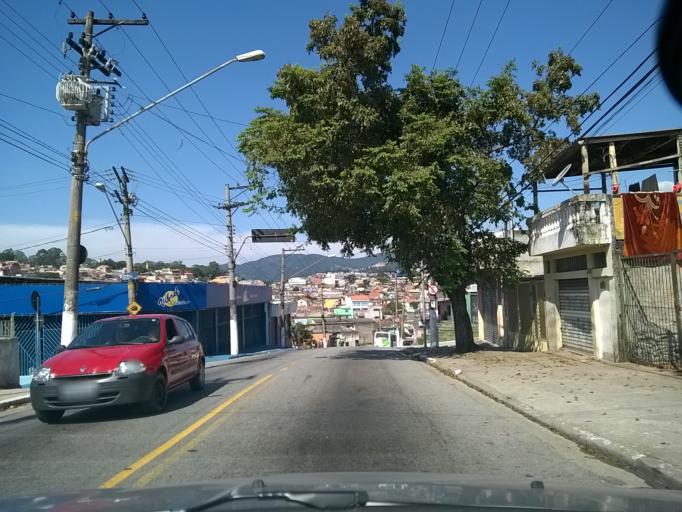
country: BR
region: Sao Paulo
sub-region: Caieiras
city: Caieiras
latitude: -23.4066
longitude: -46.7660
